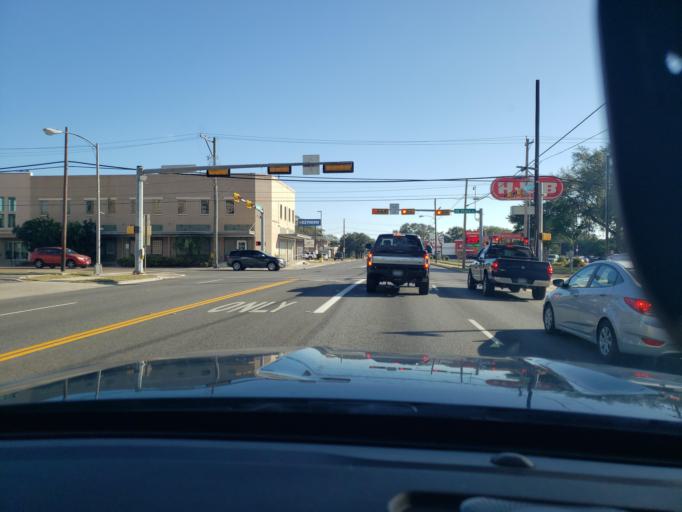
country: US
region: Texas
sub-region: Bee County
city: Beeville
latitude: 28.4010
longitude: -97.7480
